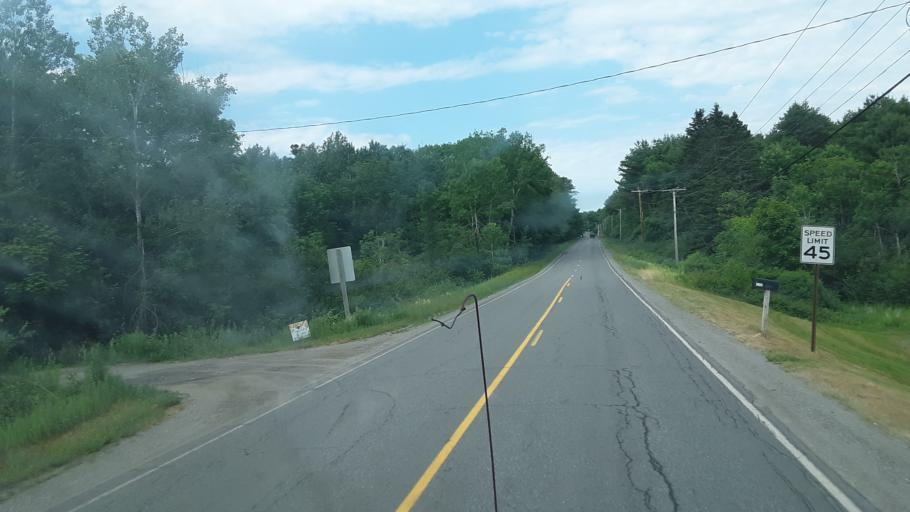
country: US
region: Maine
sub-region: Penobscot County
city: Hampden
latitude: 44.7313
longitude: -68.8639
